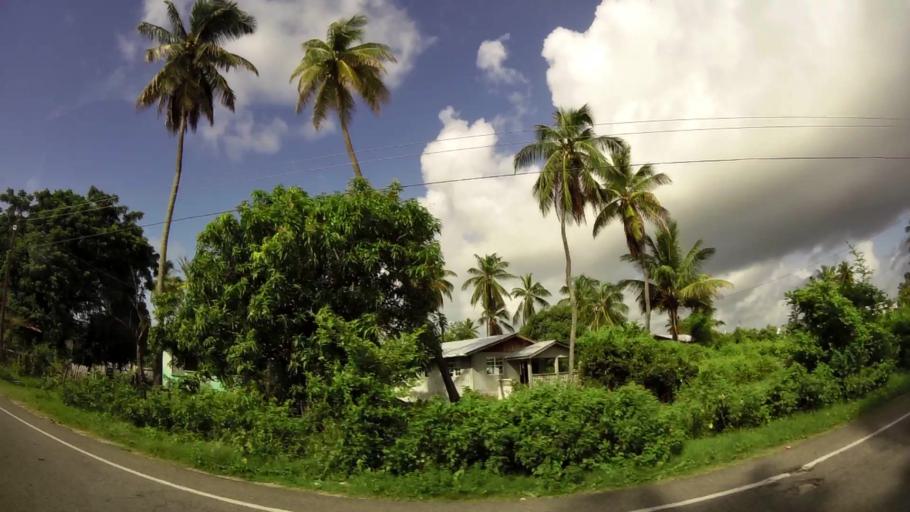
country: GY
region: Demerara-Mahaica
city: Mahaica Village
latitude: 6.7721
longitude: -57.9982
